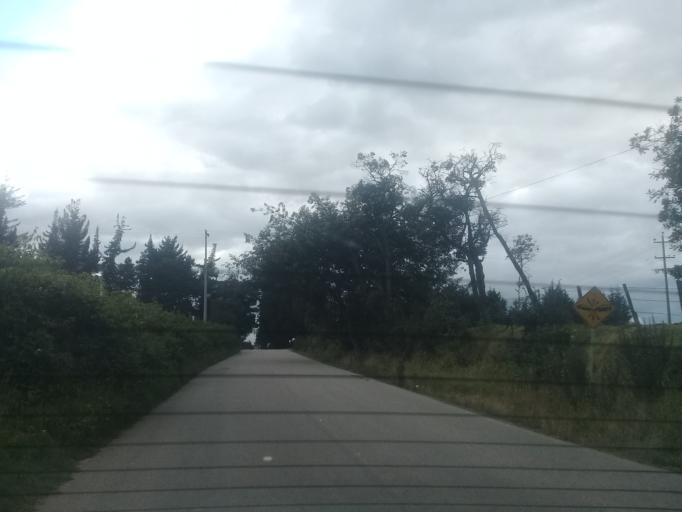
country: CO
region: Cundinamarca
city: Subachoque
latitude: 4.9303
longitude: -74.1461
